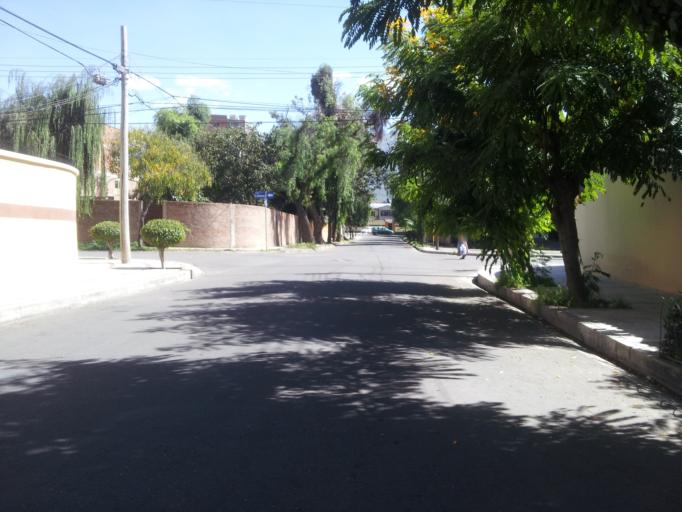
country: BO
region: Cochabamba
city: Cochabamba
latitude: -17.3778
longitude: -66.1746
